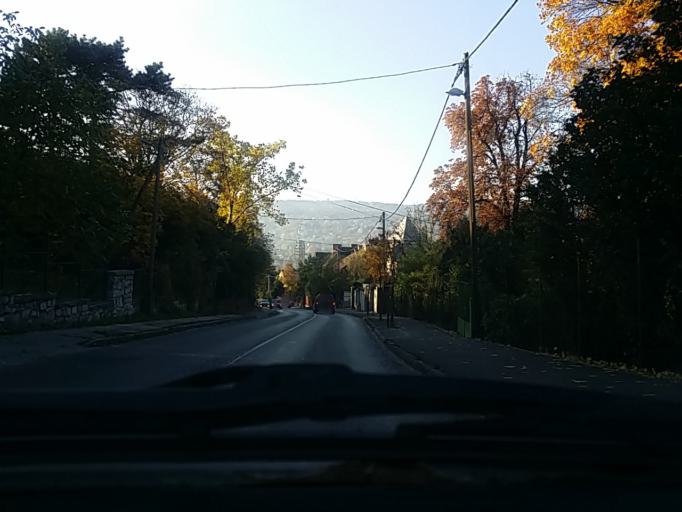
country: HU
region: Budapest
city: Budapest II. keruelet
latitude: 47.5280
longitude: 18.9954
